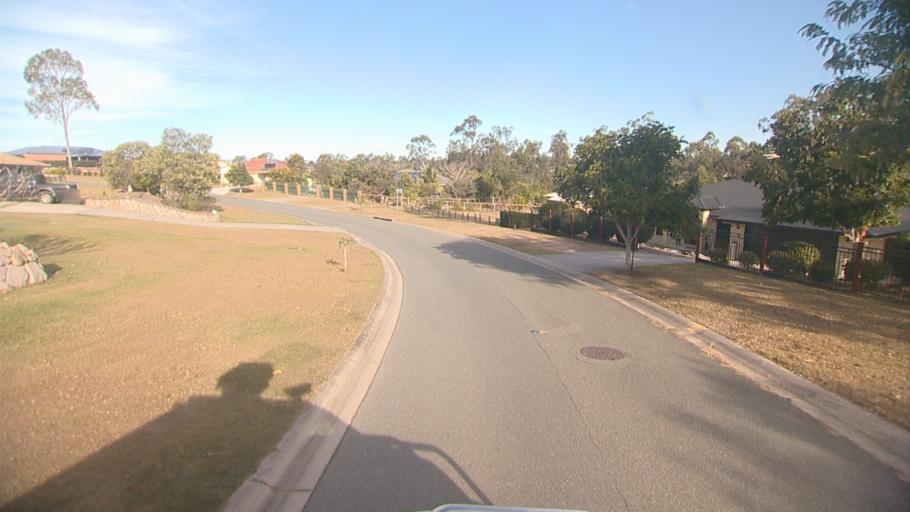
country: AU
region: Queensland
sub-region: Logan
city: North Maclean
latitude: -27.7977
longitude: 152.9572
